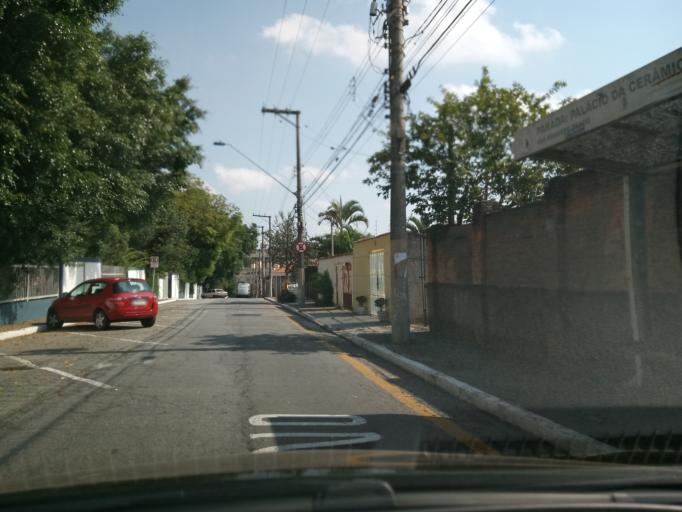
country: BR
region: Sao Paulo
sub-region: Sao Caetano Do Sul
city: Sao Caetano do Sul
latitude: -23.6324
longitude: -46.5752
